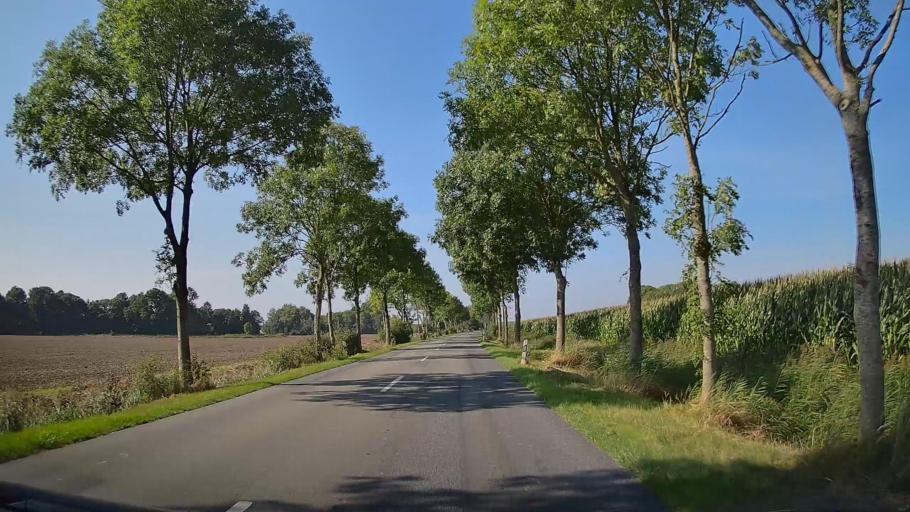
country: DE
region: Lower Saxony
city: Wremen
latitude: 53.6294
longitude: 8.5113
